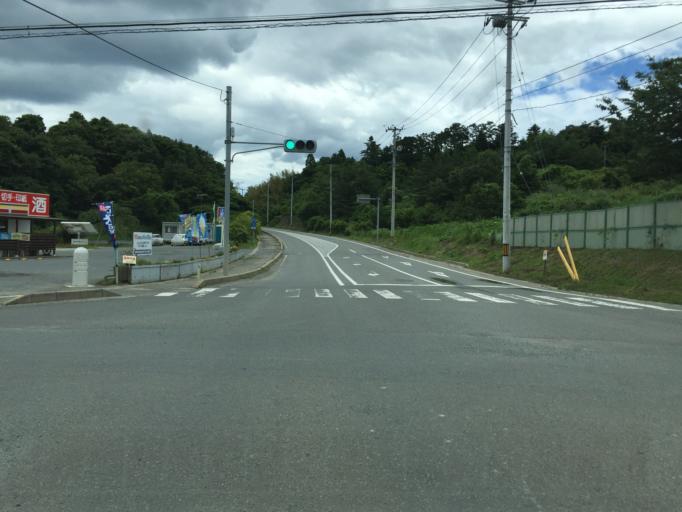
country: JP
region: Fukushima
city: Namie
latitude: 37.6516
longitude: 141.0126
